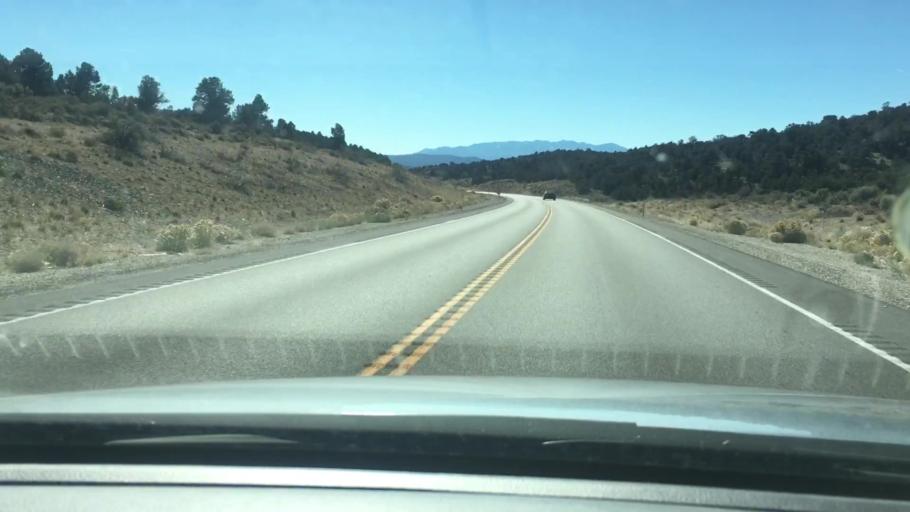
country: US
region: Nevada
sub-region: White Pine County
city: Ely
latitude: 39.2050
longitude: -114.9934
